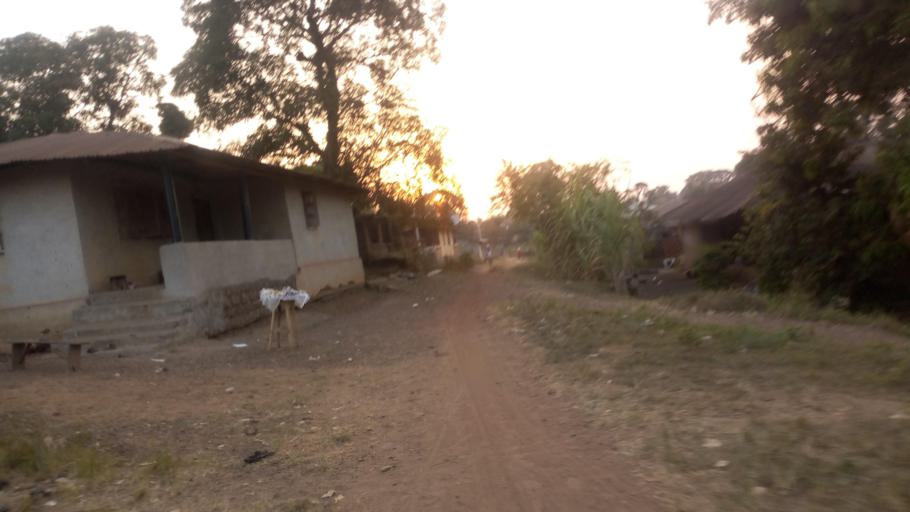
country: SL
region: Southern Province
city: Mogbwemo
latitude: 7.6077
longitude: -12.1781
